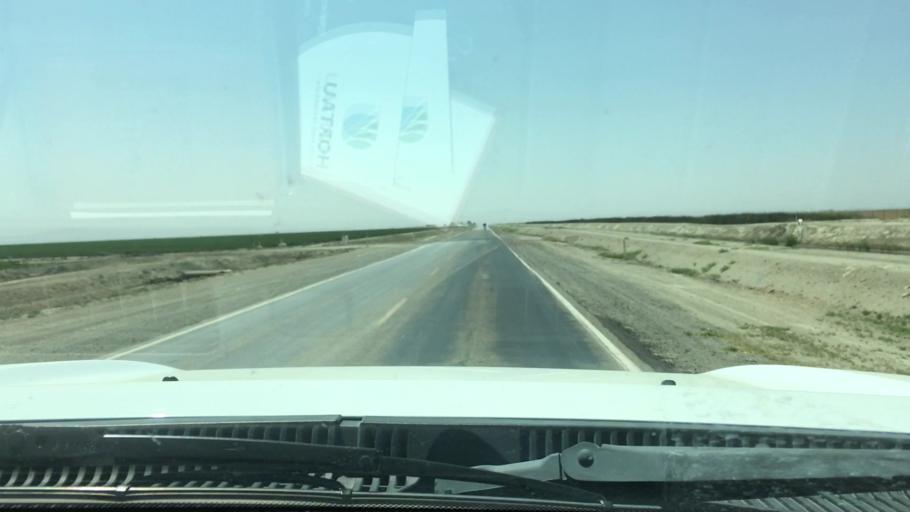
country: US
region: California
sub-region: Tulare County
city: Alpaugh
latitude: 35.9343
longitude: -119.6080
